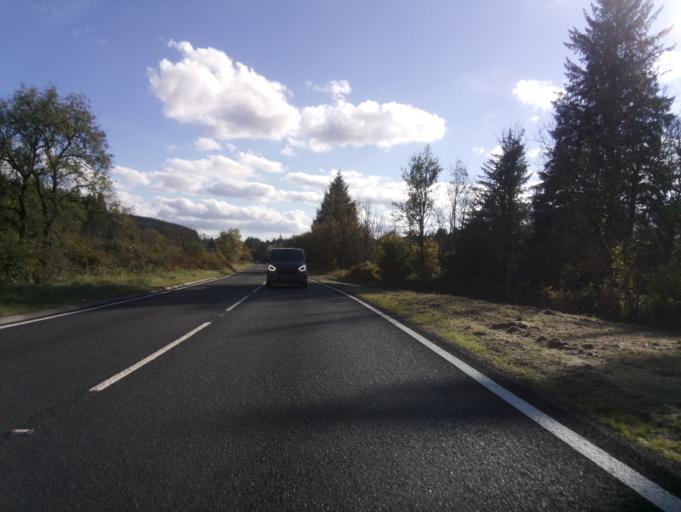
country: GB
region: Wales
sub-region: Merthyr Tydfil County Borough
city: Merthyr Tydfil
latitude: 51.8118
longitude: -3.4444
